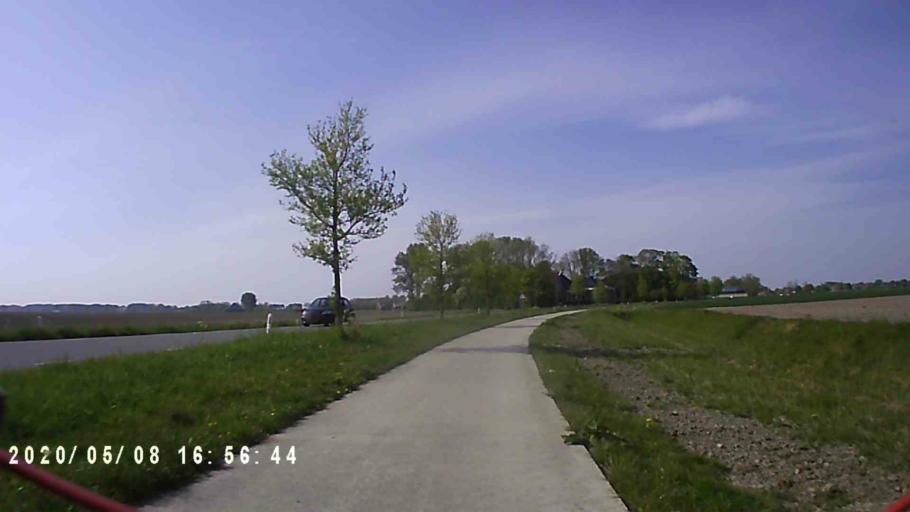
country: NL
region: Groningen
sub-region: Gemeente Bedum
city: Bedum
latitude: 53.3941
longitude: 6.6156
